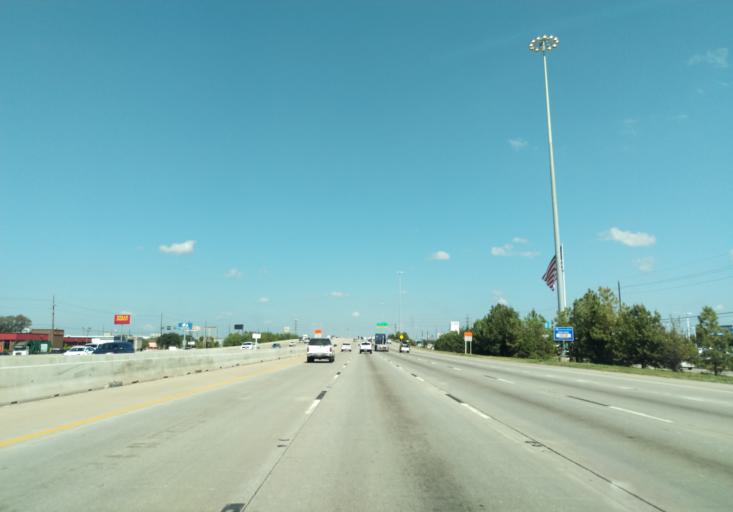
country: US
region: Texas
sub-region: Harris County
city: Spring
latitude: 30.0164
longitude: -95.4283
